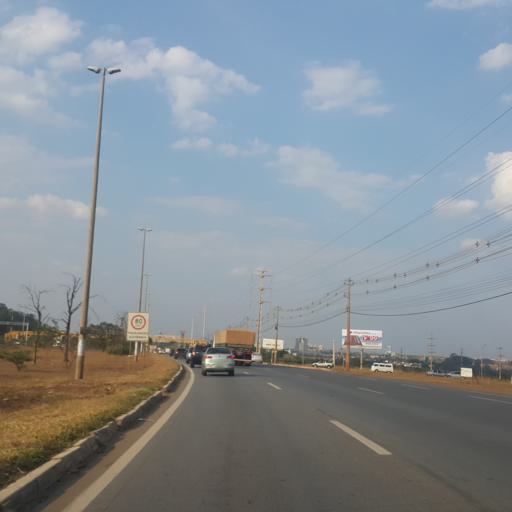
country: BR
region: Federal District
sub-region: Brasilia
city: Brasilia
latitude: -15.8809
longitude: -48.0553
